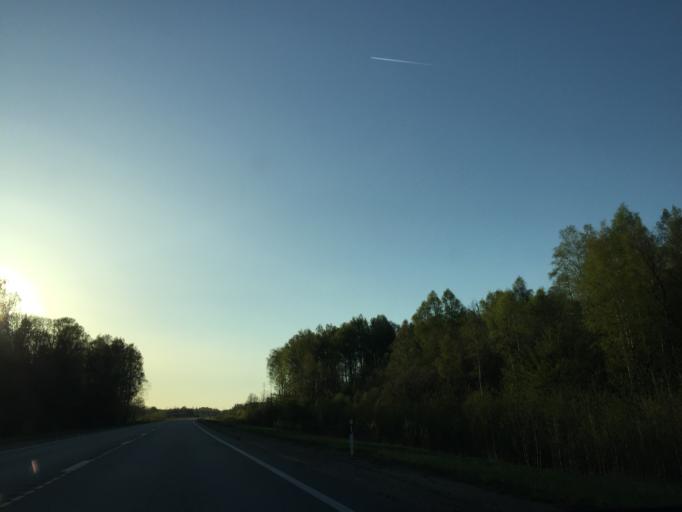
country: LV
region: Aizkraukles Rajons
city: Aizkraukle
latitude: 56.7090
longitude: 25.2273
